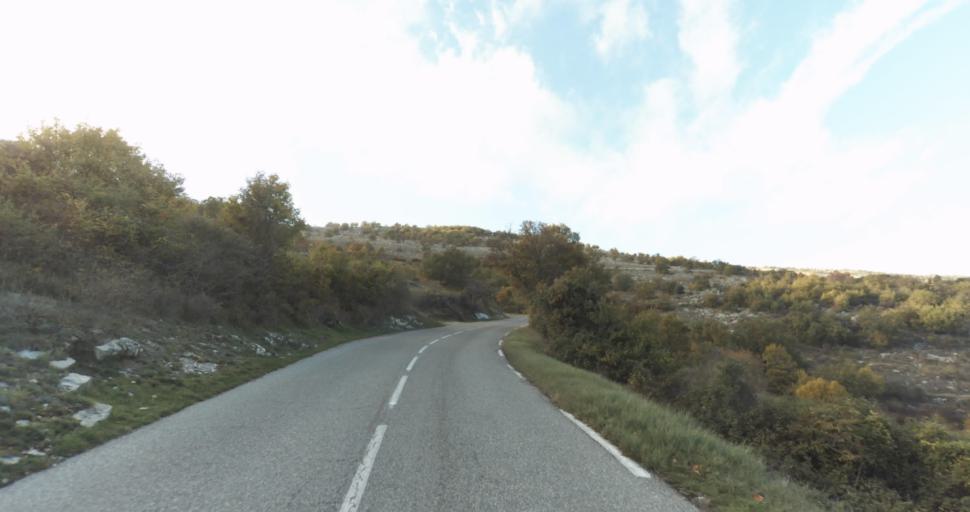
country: FR
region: Provence-Alpes-Cote d'Azur
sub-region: Departement des Alpes-Maritimes
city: Vence
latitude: 43.7599
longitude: 7.0856
